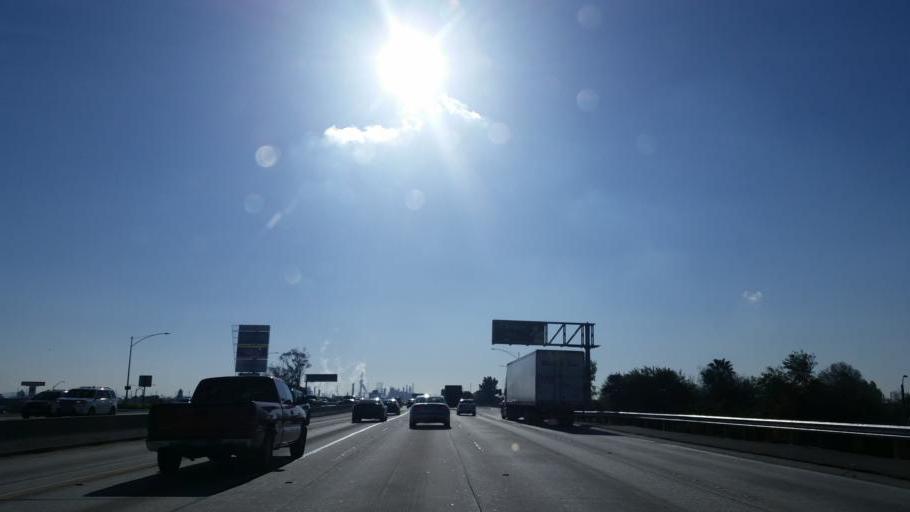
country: US
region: California
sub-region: Los Angeles County
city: Carson
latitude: 33.8327
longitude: -118.2571
